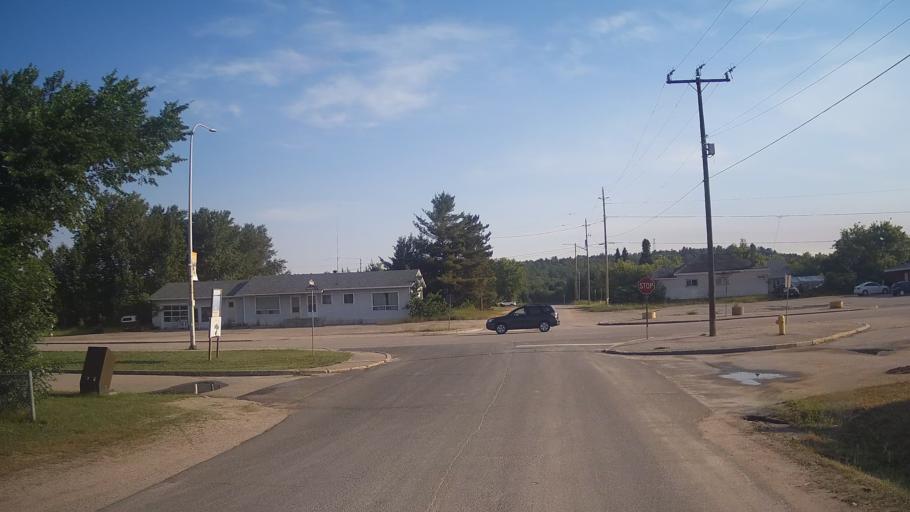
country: CA
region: Ontario
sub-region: Rainy River District
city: Atikokan
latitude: 49.4161
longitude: -91.6646
